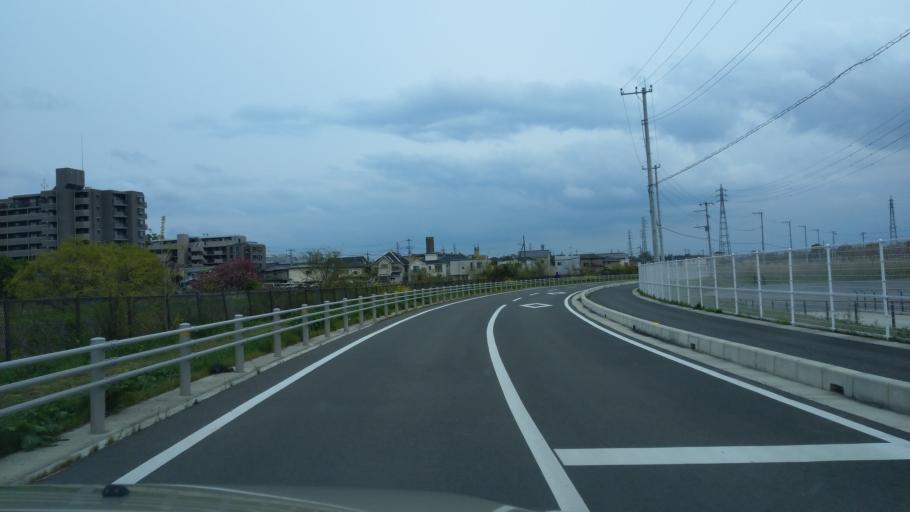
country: JP
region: Saitama
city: Ageoshimo
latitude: 35.9418
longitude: 139.5994
